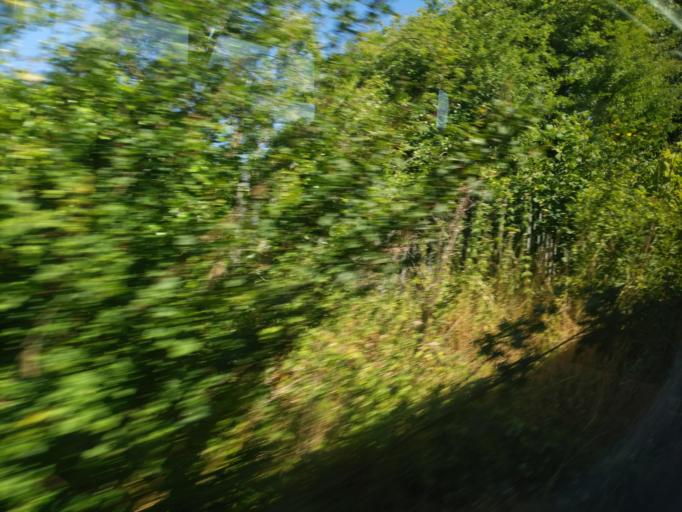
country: GB
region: England
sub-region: Devon
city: Kingskerswell
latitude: 50.4978
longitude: -3.5832
